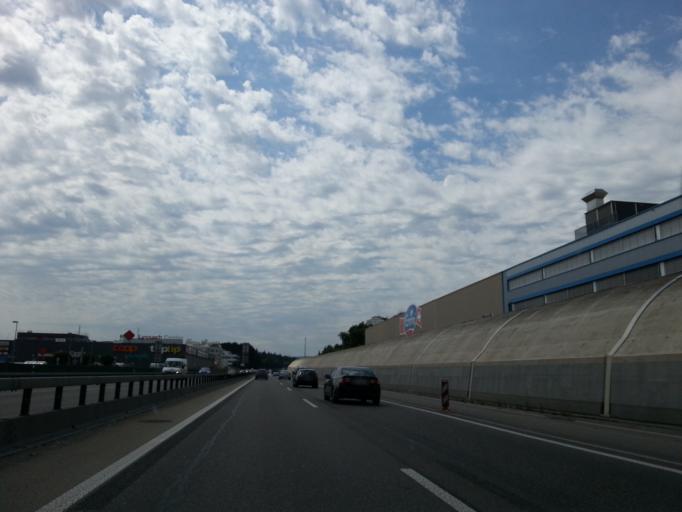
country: CH
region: Bern
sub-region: Emmental District
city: Lyssach
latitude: 47.0748
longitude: 7.5687
